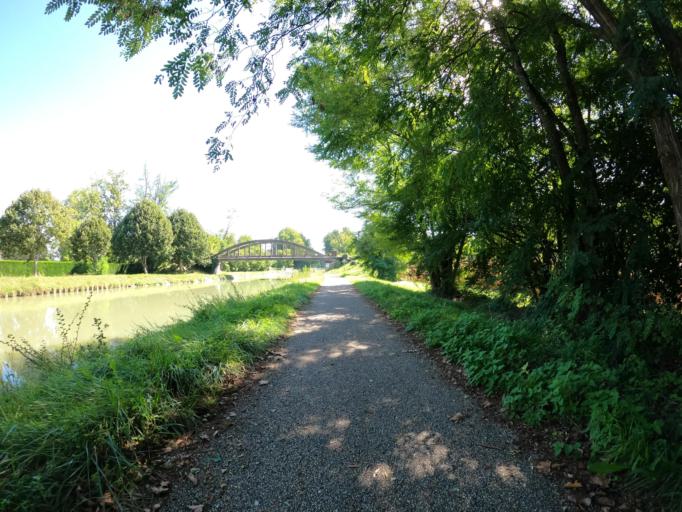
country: FR
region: Midi-Pyrenees
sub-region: Departement du Tarn-et-Garonne
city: Lamagistere
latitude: 44.1222
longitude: 0.8451
